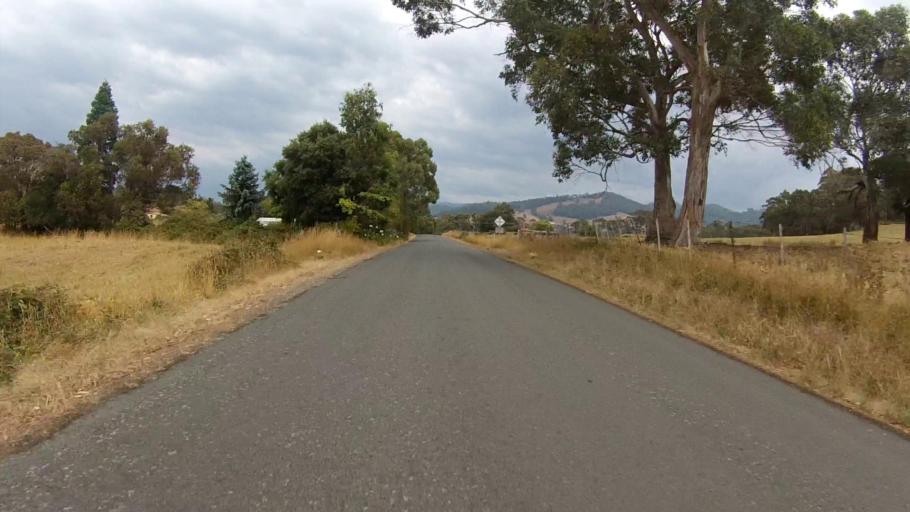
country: AU
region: Tasmania
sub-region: Huon Valley
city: Cygnet
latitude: -43.1834
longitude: 147.1100
